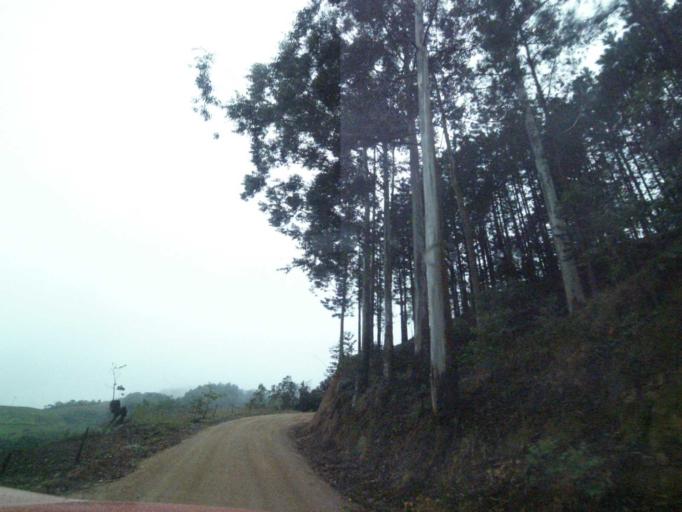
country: BR
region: Santa Catarina
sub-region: Anitapolis
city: Anitapolis
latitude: -27.9095
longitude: -49.1196
